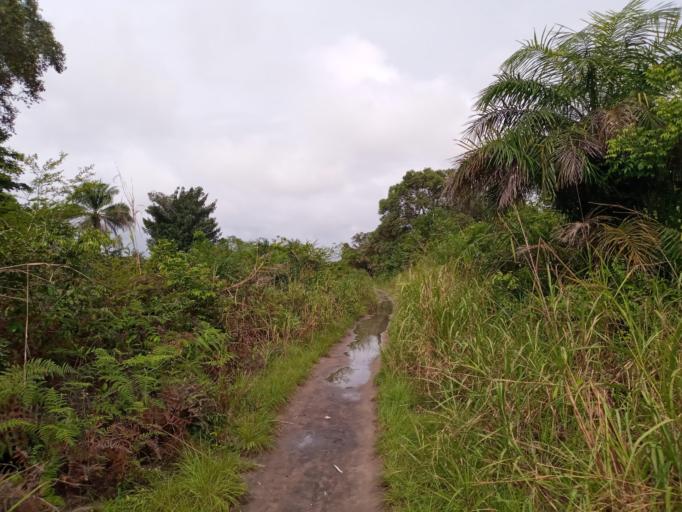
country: SL
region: Southern Province
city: Bonthe
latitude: 7.5190
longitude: -12.5396
